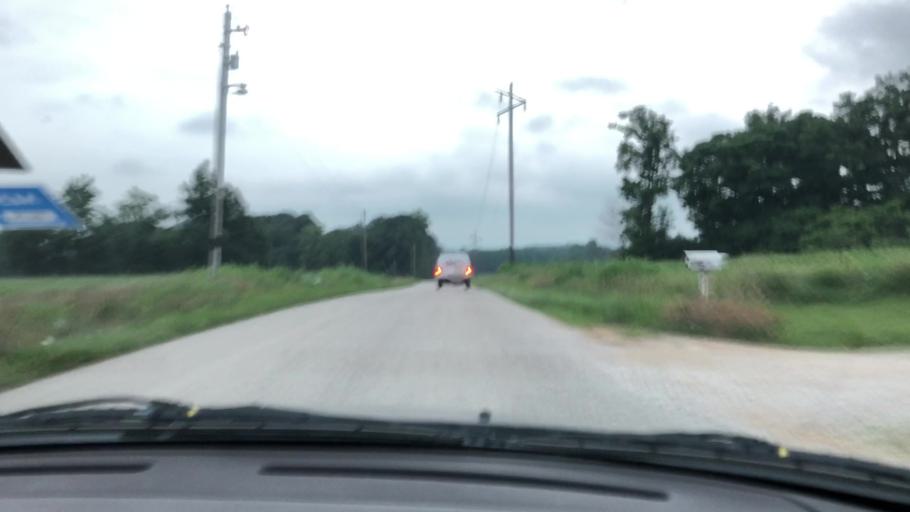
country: US
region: Indiana
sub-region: Greene County
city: Linton
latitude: 38.9834
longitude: -87.2981
